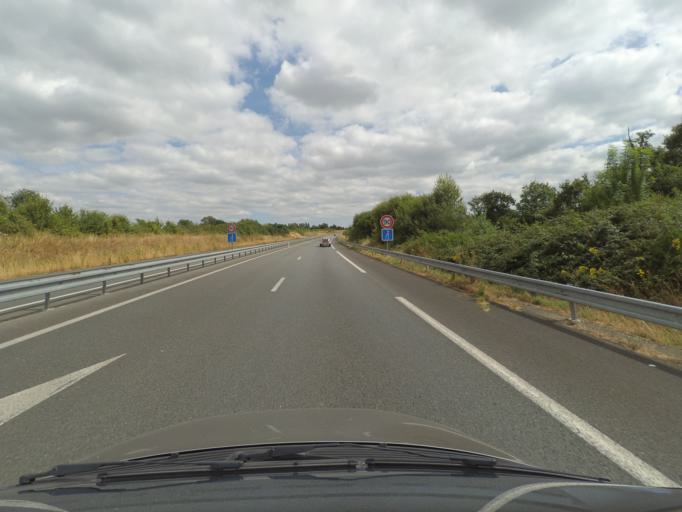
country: FR
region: Pays de la Loire
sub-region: Departement de Maine-et-Loire
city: Vezins
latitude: 47.1249
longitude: -0.7048
